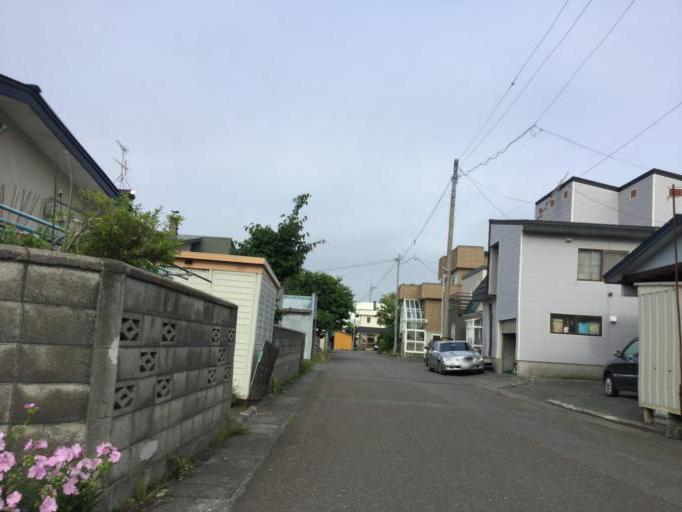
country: JP
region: Hokkaido
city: Wakkanai
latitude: 45.3940
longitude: 141.7038
